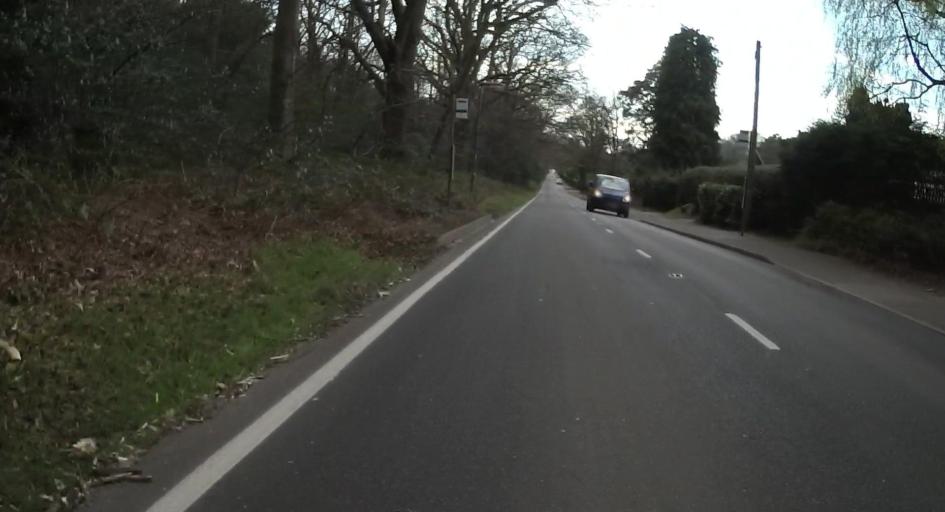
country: GB
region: England
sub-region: Surrey
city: Camberley
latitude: 51.3243
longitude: -0.7105
